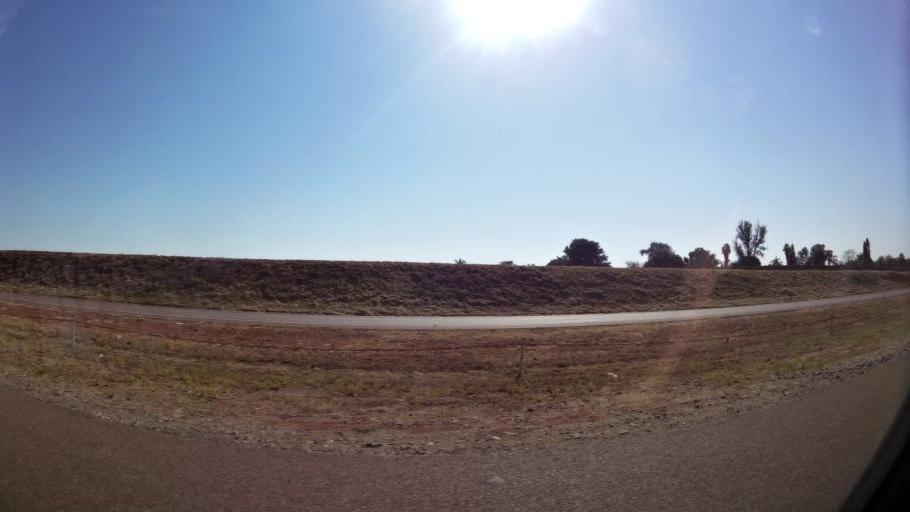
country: ZA
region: Gauteng
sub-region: City of Tshwane Metropolitan Municipality
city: Pretoria
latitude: -25.6543
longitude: 28.1166
